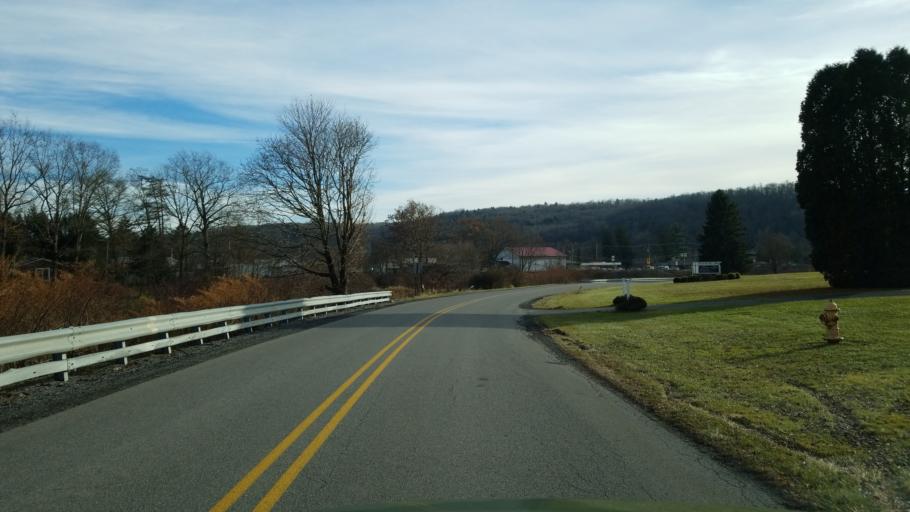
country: US
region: Pennsylvania
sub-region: Clearfield County
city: Hyde
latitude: 41.0118
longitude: -78.4516
